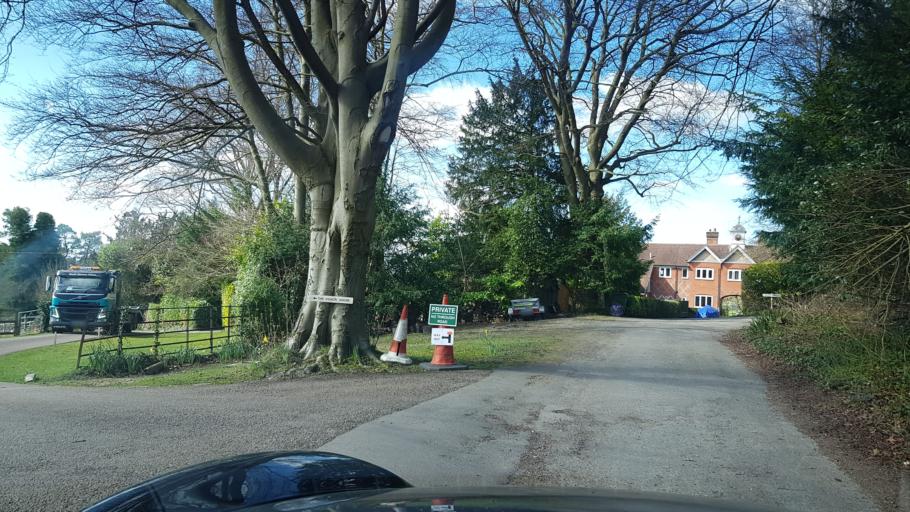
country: GB
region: England
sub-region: Surrey
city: Godalming
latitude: 51.2250
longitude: -0.6401
